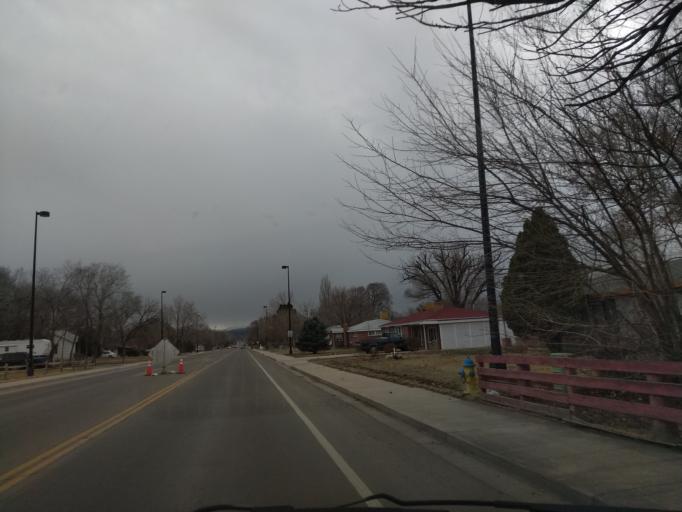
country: US
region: Colorado
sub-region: Mesa County
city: Fruitvale
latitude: 39.0843
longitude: -108.5152
